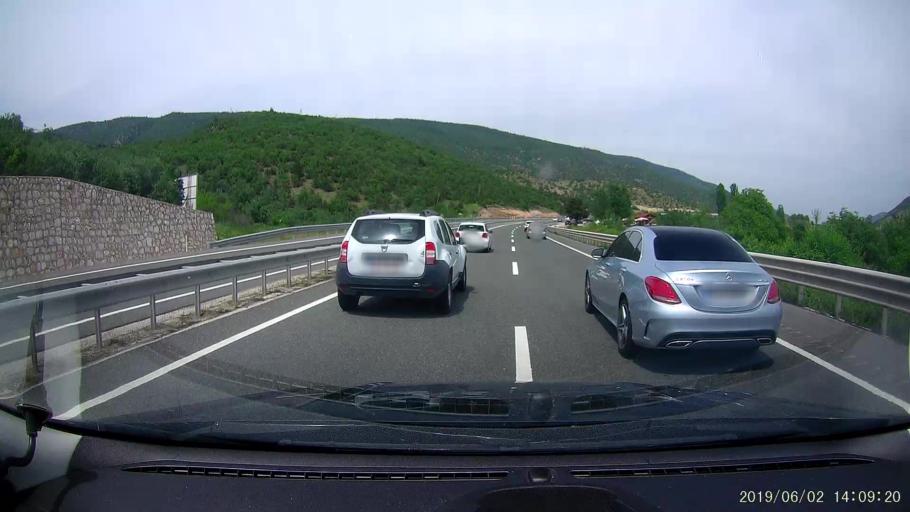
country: TR
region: Cankiri
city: Ilgaz
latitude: 40.8933
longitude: 33.7405
